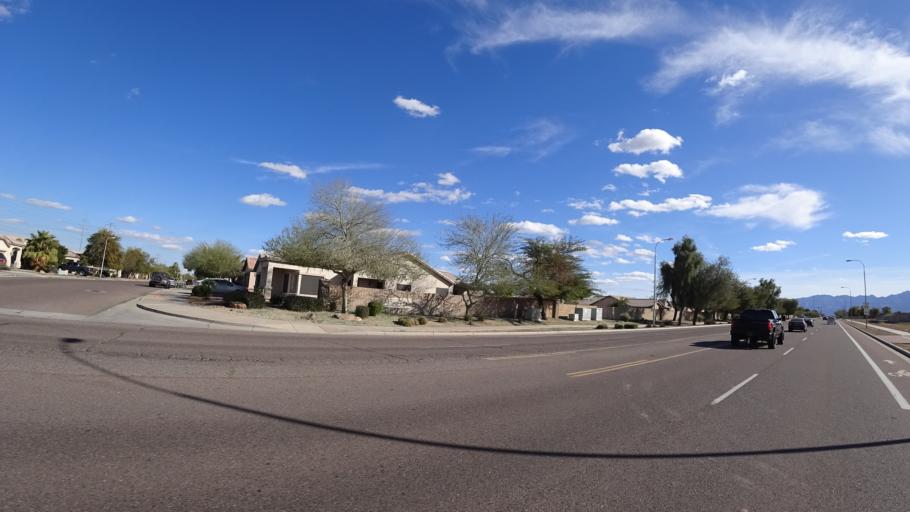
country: US
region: Arizona
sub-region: Maricopa County
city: Tolleson
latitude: 33.4152
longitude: -112.2214
